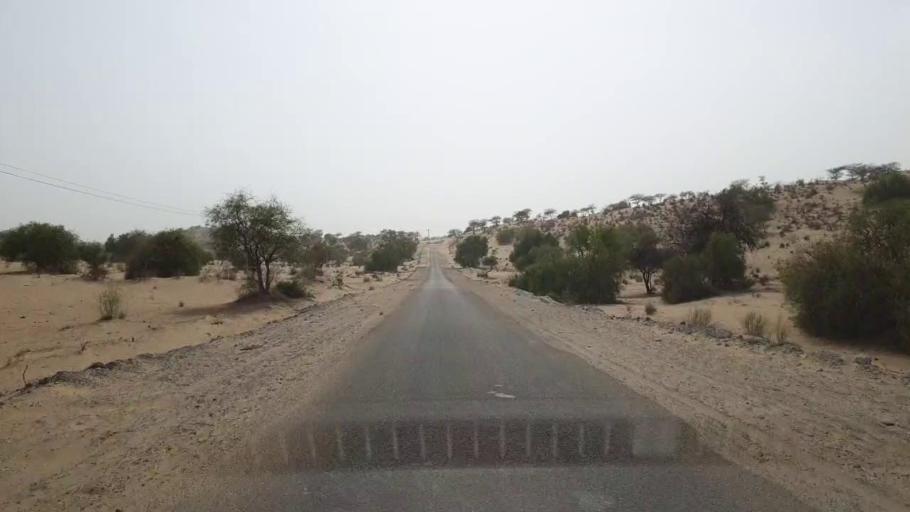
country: PK
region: Sindh
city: Mithi
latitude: 24.6223
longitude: 69.9077
